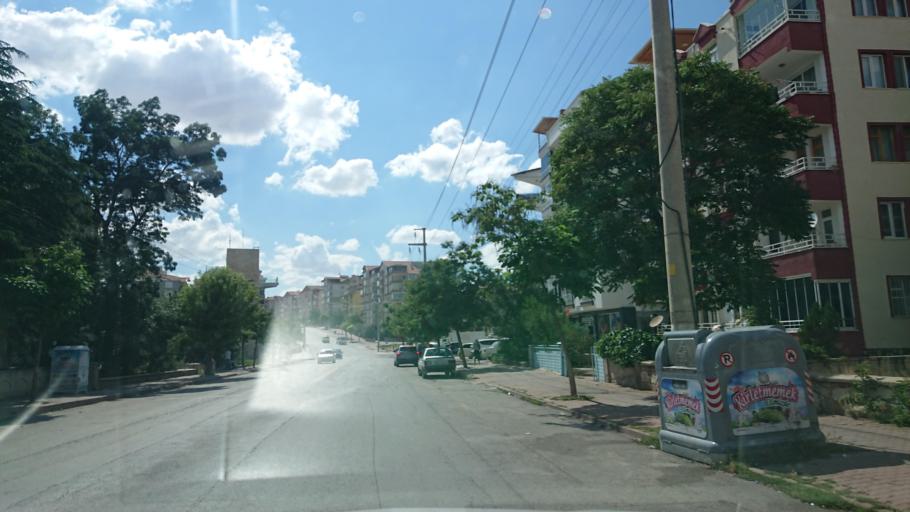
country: TR
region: Kirsehir
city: Kirsehir
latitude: 39.1549
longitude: 34.1557
